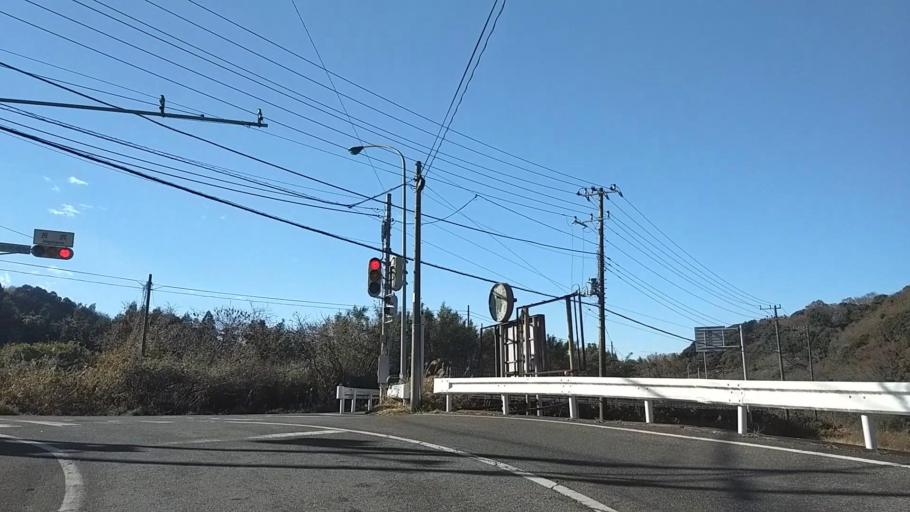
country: JP
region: Chiba
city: Futtsu
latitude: 35.2298
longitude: 139.8763
